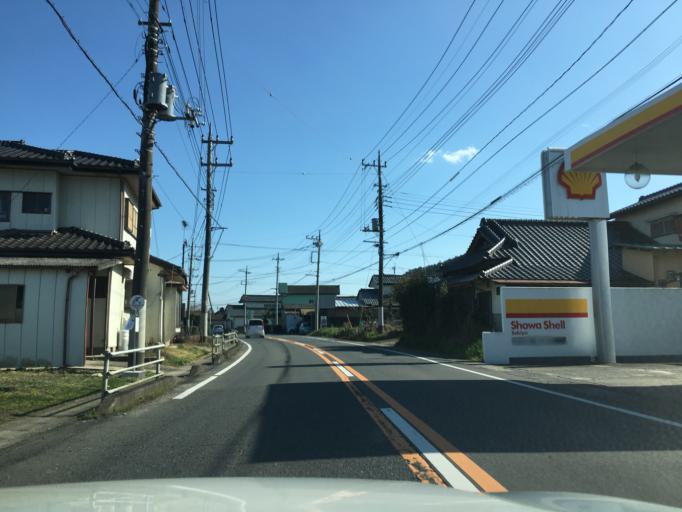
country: JP
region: Ibaraki
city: Omiya
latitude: 36.5419
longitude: 140.3366
